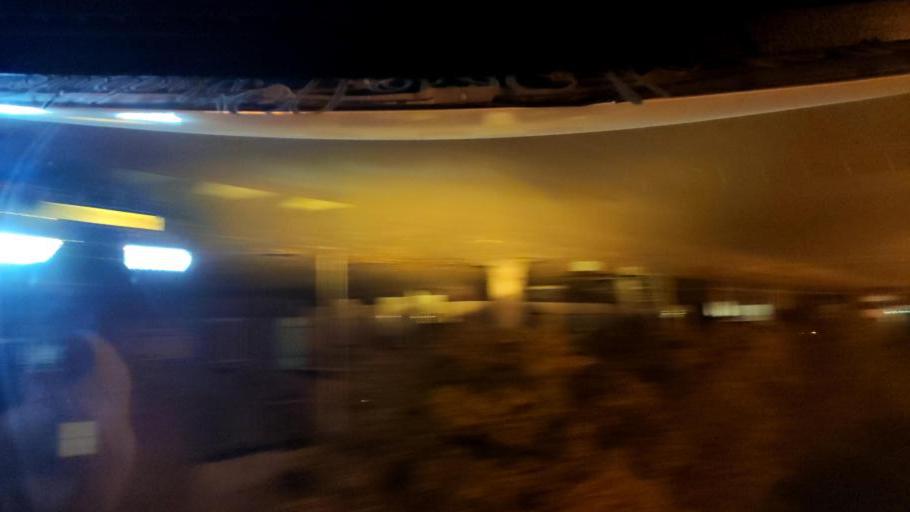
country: RU
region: Voronezj
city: Voronezh
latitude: 51.6753
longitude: 39.1566
